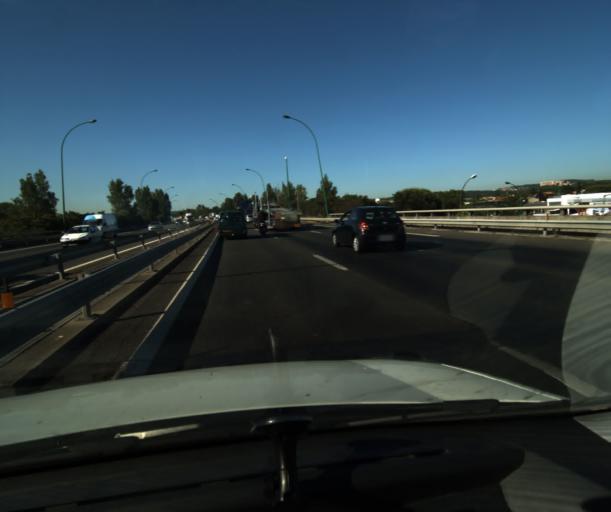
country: FR
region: Midi-Pyrenees
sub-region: Departement de la Haute-Garonne
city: Ramonville-Saint-Agne
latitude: 43.5728
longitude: 1.4950
